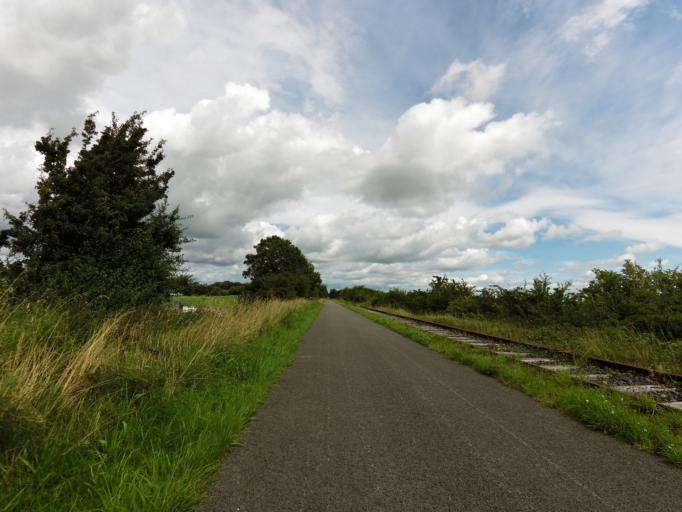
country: IE
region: Leinster
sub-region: An Iarmhi
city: Kilbeggan
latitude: 53.4709
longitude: -7.4918
